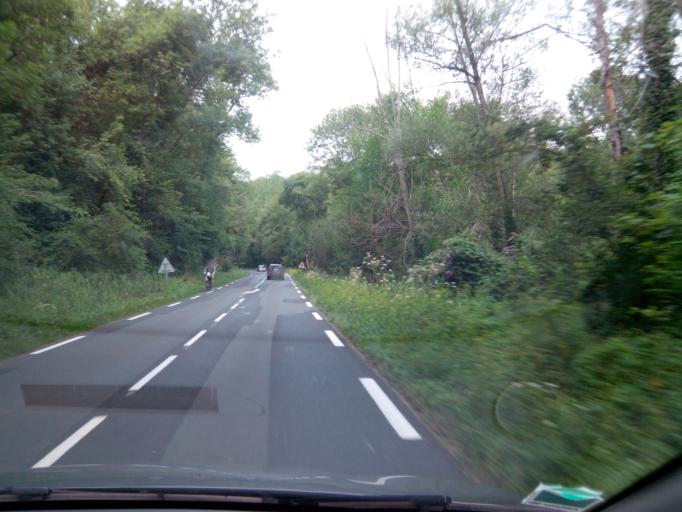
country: FR
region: Aquitaine
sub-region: Departement de la Dordogne
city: Carsac-Aillac
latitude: 44.8682
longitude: 1.2823
